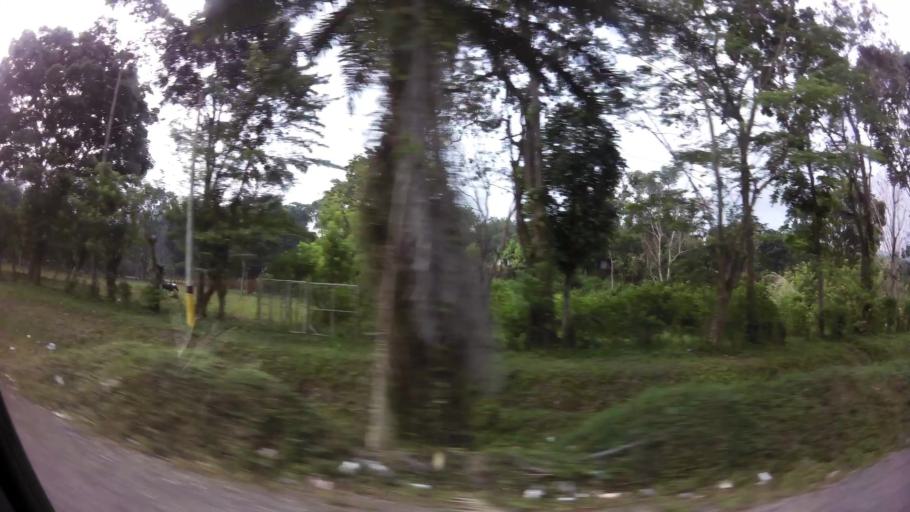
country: HN
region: Yoro
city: Guaimitas
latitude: 15.5124
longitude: -87.6746
